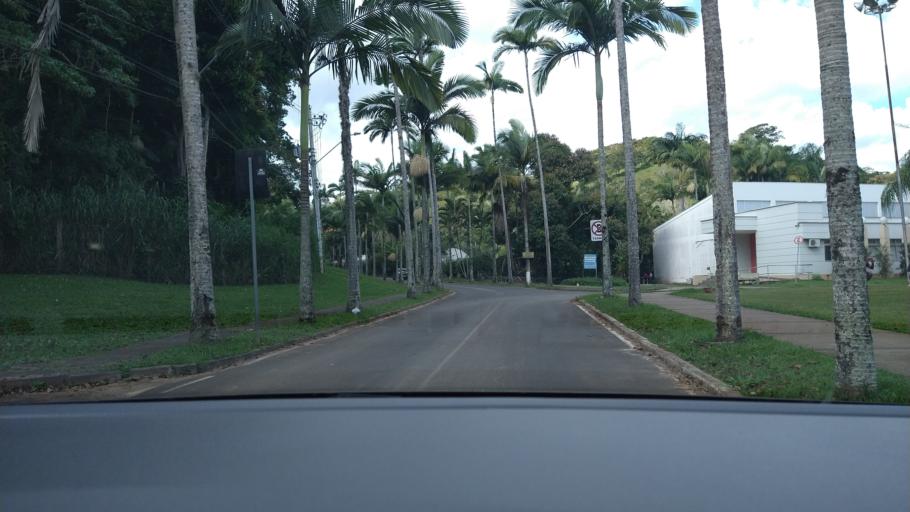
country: BR
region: Minas Gerais
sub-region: Vicosa
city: Vicosa
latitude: -20.7606
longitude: -42.8644
